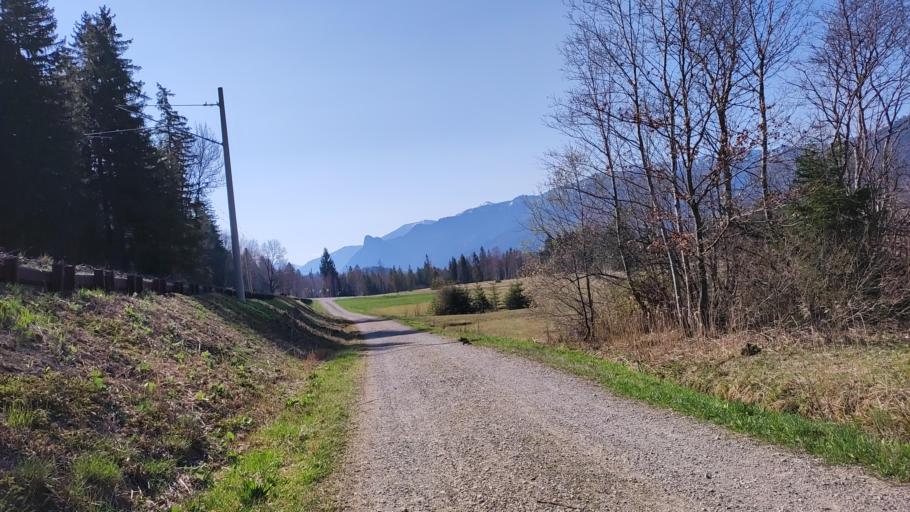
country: DE
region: Bavaria
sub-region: Upper Bavaria
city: Unterammergau
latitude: 47.6395
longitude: 11.0253
